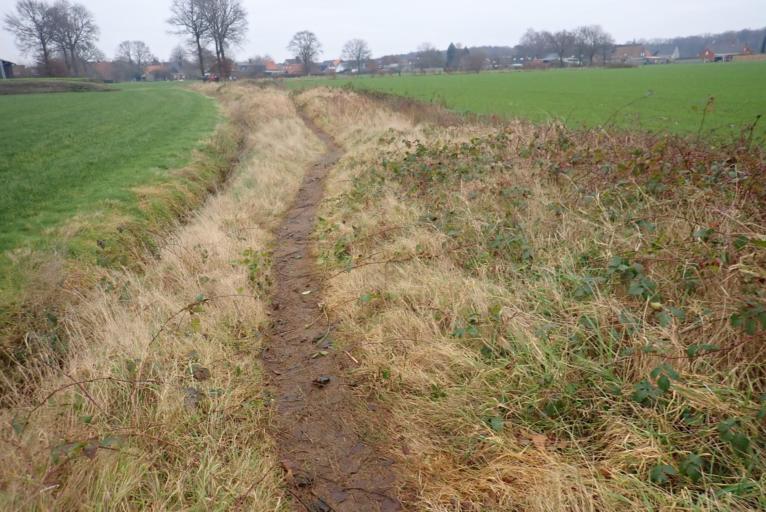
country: BE
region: Flanders
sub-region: Provincie Antwerpen
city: Vorselaar
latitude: 51.2199
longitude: 4.7767
